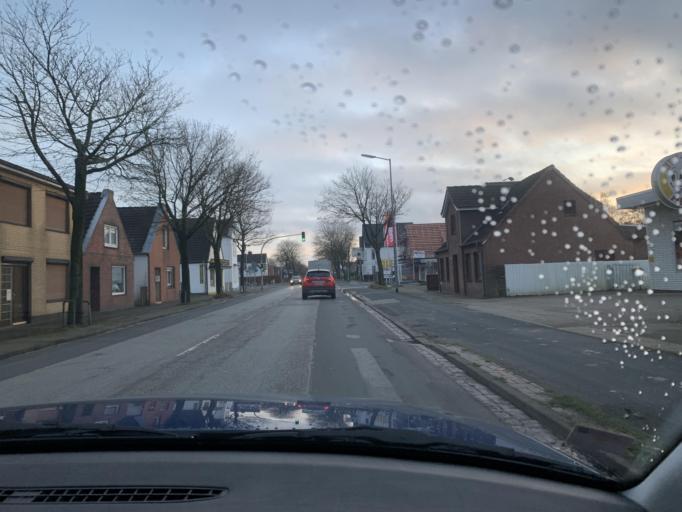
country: DE
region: Schleswig-Holstein
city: Heide
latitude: 54.1895
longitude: 9.0900
